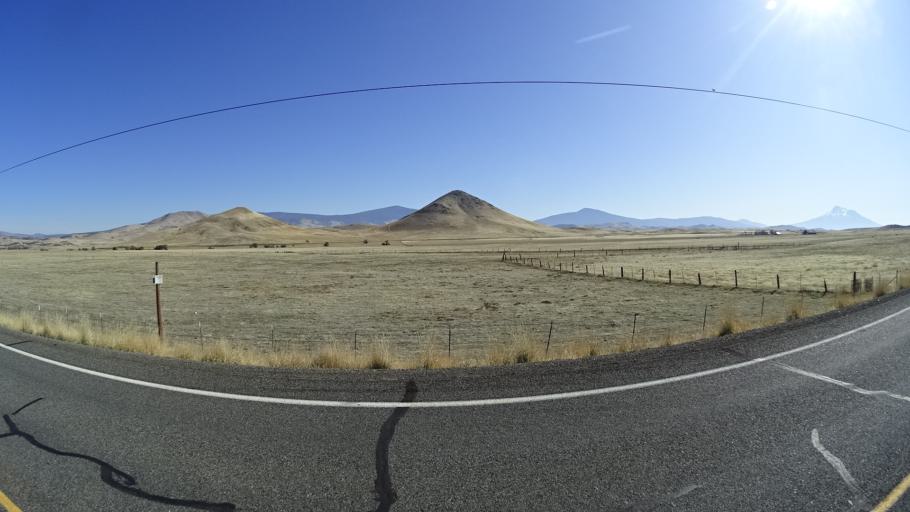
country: US
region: California
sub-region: Siskiyou County
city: Montague
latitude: 41.8228
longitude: -122.4962
